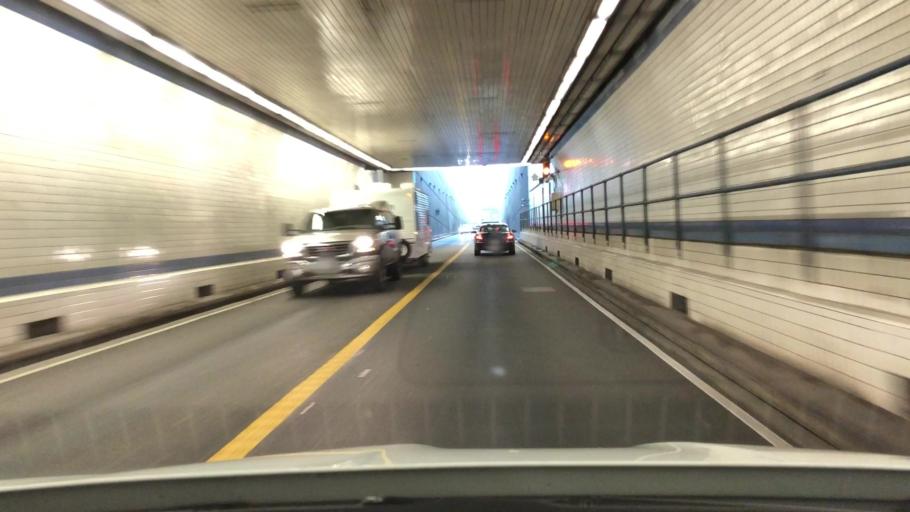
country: US
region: Virginia
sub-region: City of Virginia Beach
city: Virginia Beach
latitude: 37.0367
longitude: -76.0768
